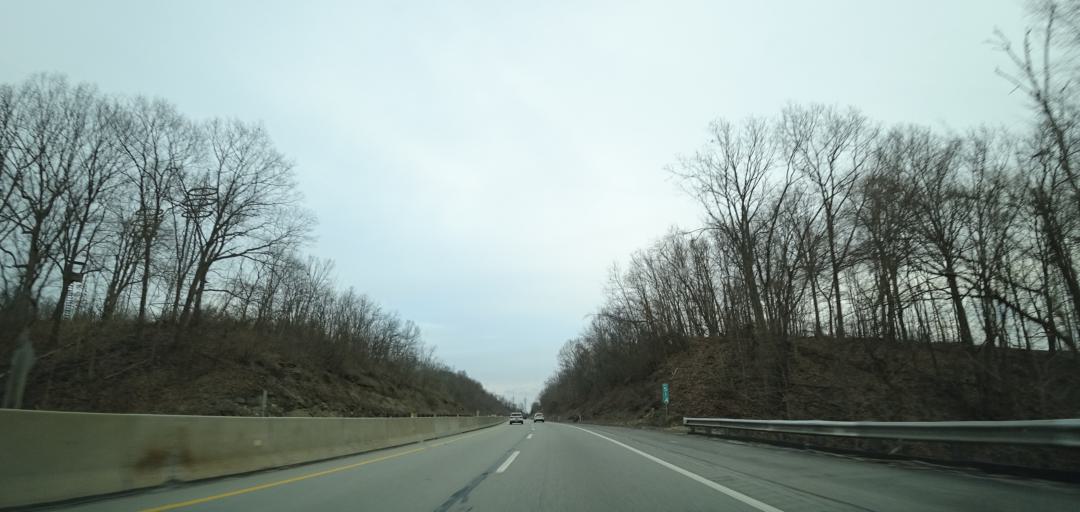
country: US
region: Pennsylvania
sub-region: Allegheny County
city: Springdale
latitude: 40.5031
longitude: -79.7888
